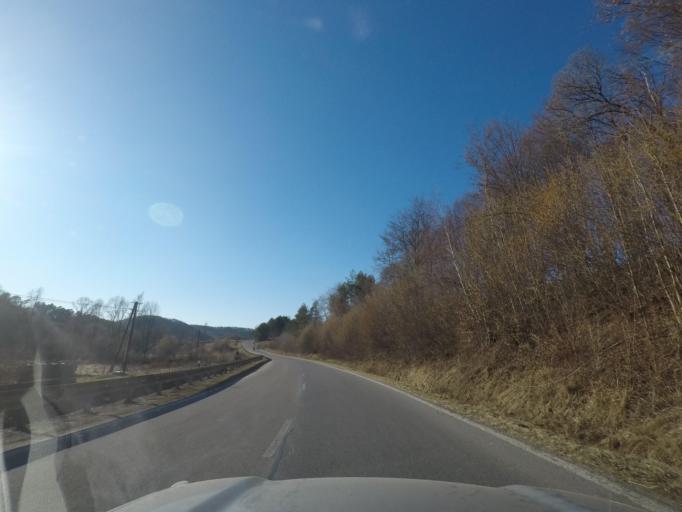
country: SK
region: Presovsky
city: Medzilaborce
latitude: 49.2491
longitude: 21.9270
